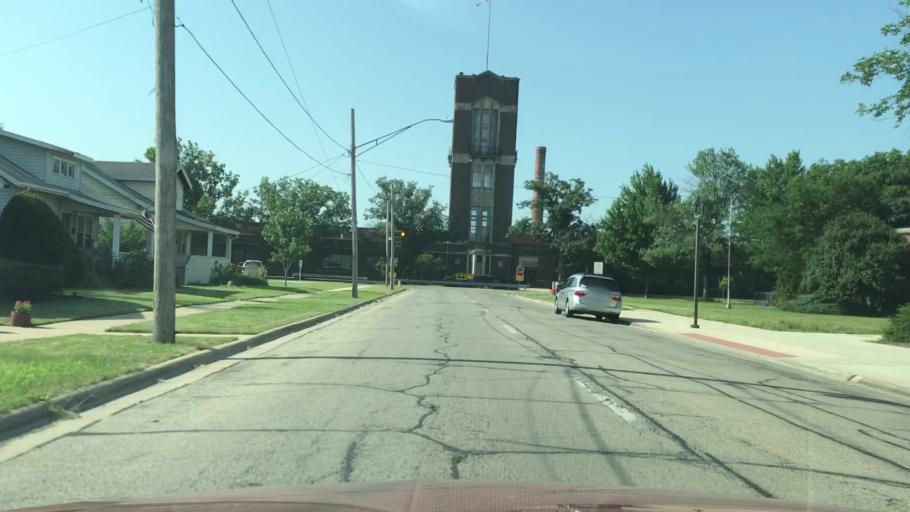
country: US
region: Illinois
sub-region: Winnebago County
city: Rockford
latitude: 42.2420
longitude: -89.0825
